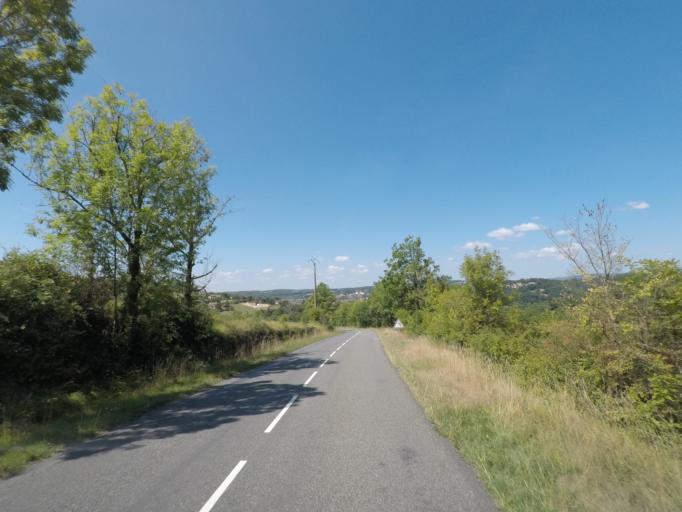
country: FR
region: Midi-Pyrenees
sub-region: Departement du Lot
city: Figeac
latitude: 44.6053
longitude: 2.0583
